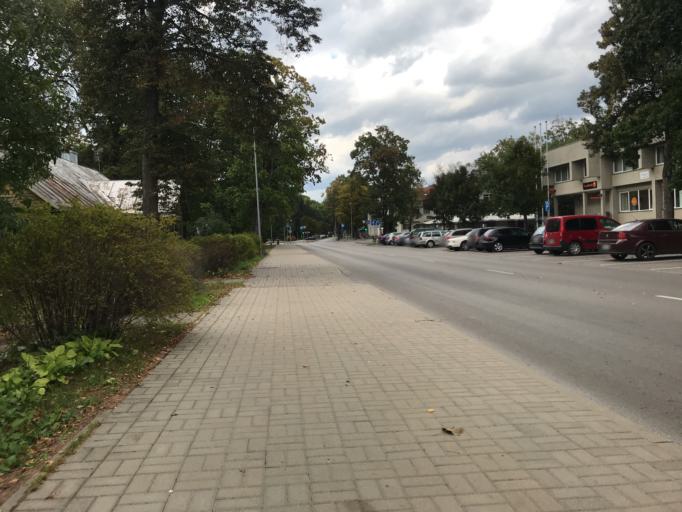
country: LT
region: Alytaus apskritis
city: Druskininkai
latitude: 54.0150
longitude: 23.9754
